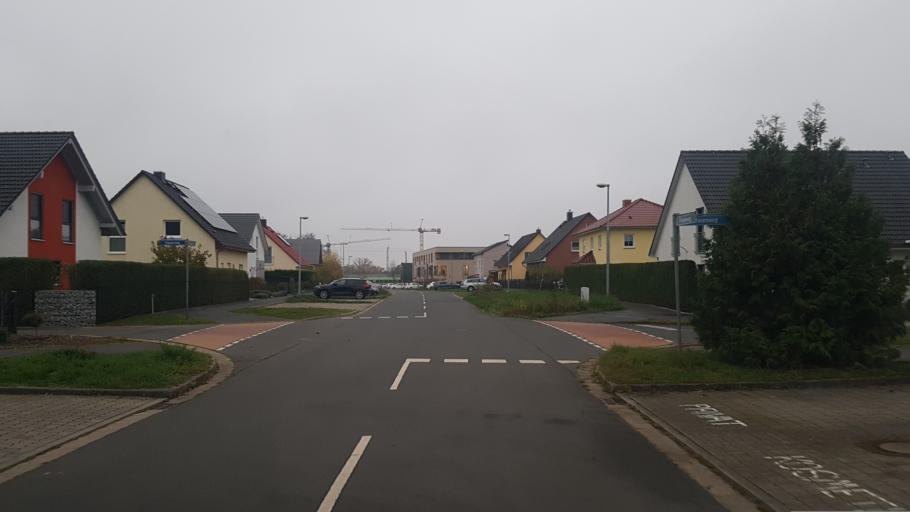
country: DE
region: Brandenburg
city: Michendorf
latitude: 52.3169
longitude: 13.0261
